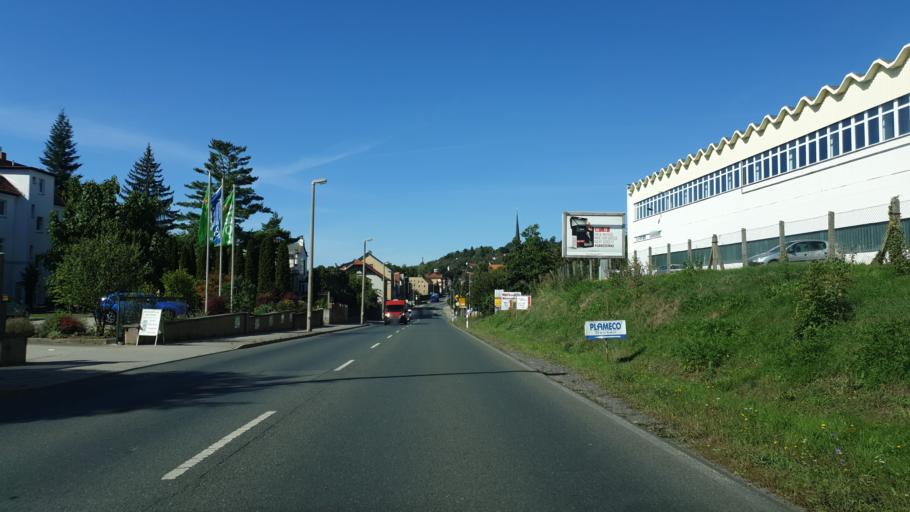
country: DE
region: Thuringia
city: Gera
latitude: 50.9169
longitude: 12.0562
